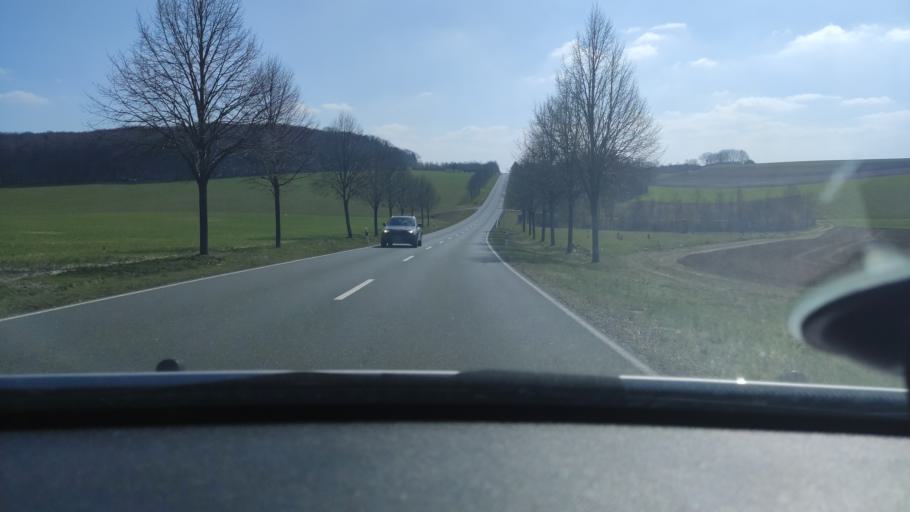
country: DE
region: Baden-Wuerttemberg
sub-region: Regierungsbezirk Stuttgart
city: Assamstadt
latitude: 49.4492
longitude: 9.6891
